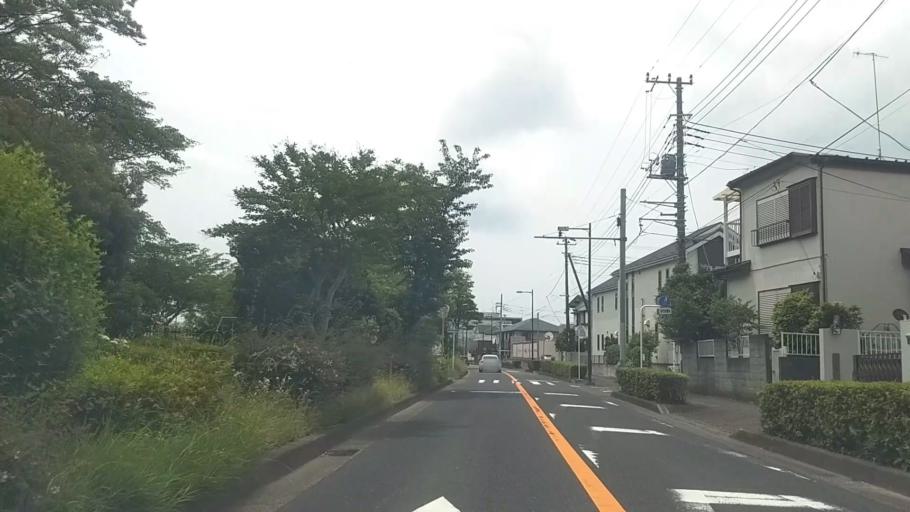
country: JP
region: Kanagawa
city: Fujisawa
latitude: 35.3457
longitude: 139.4667
